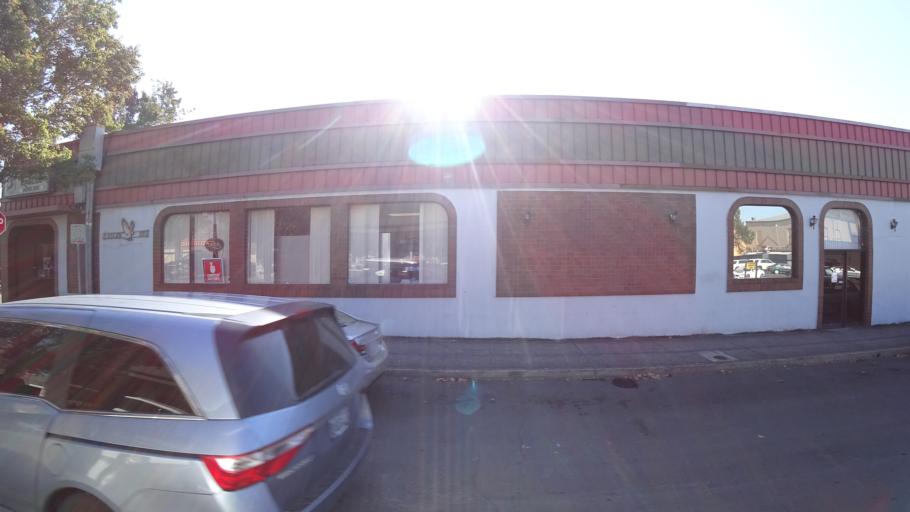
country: US
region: Oregon
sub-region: Multnomah County
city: Gresham
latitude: 45.4989
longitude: -122.4299
